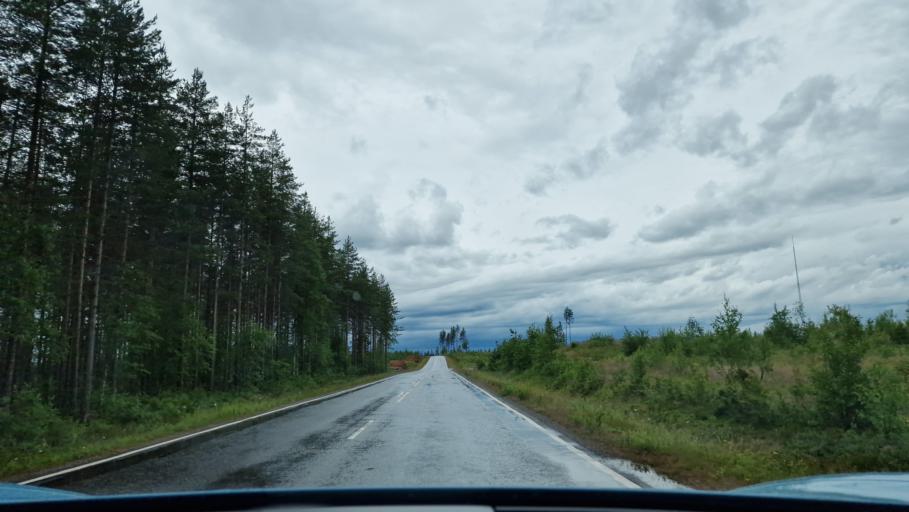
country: FI
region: Central Finland
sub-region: Saarijaervi-Viitasaari
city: Pylkoenmaeki
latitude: 62.6630
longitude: 24.5533
